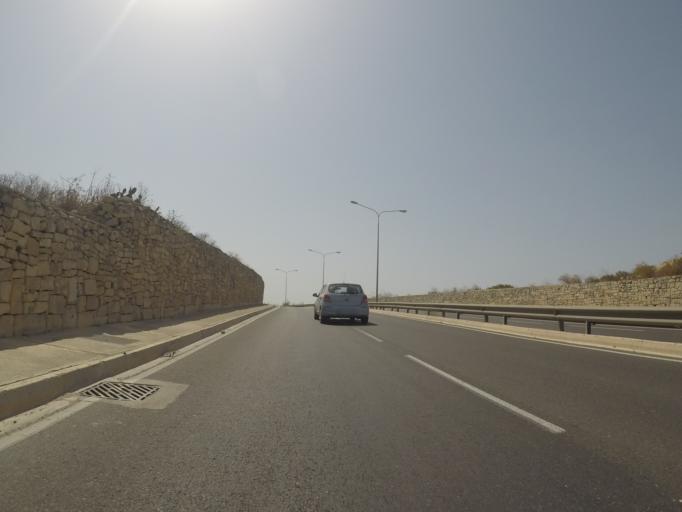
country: MT
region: L-Imdina
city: Imdina
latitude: 35.8854
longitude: 14.4118
